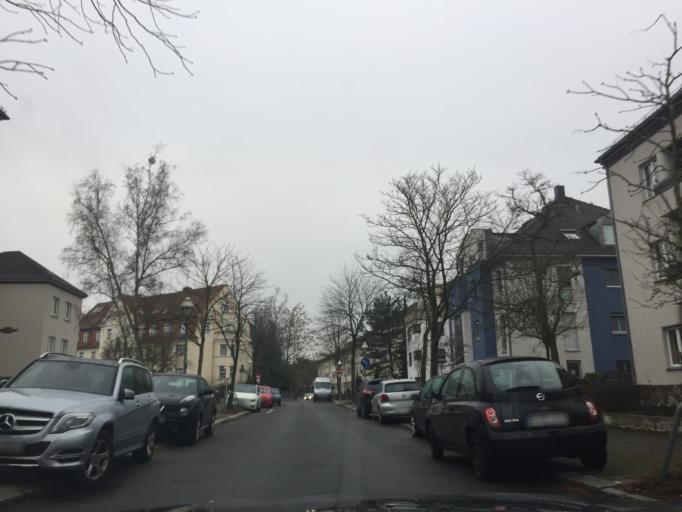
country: DE
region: Berlin
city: Westend
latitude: 52.5131
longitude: 13.2575
